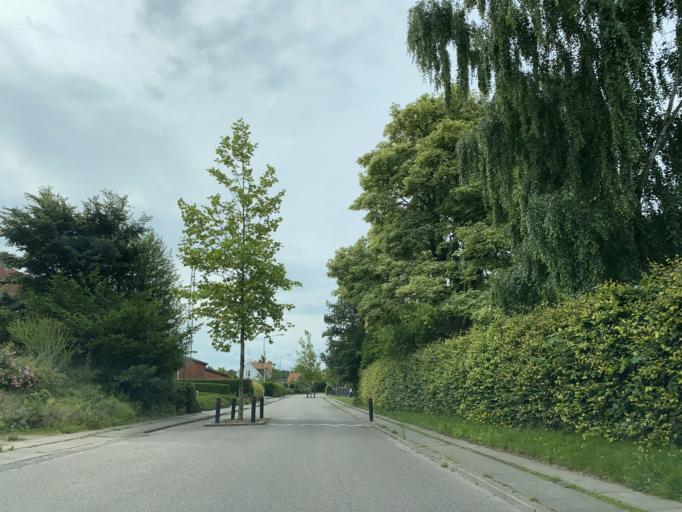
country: DK
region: South Denmark
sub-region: Sonderborg Kommune
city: Sonderborg
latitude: 54.9182
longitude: 9.8242
